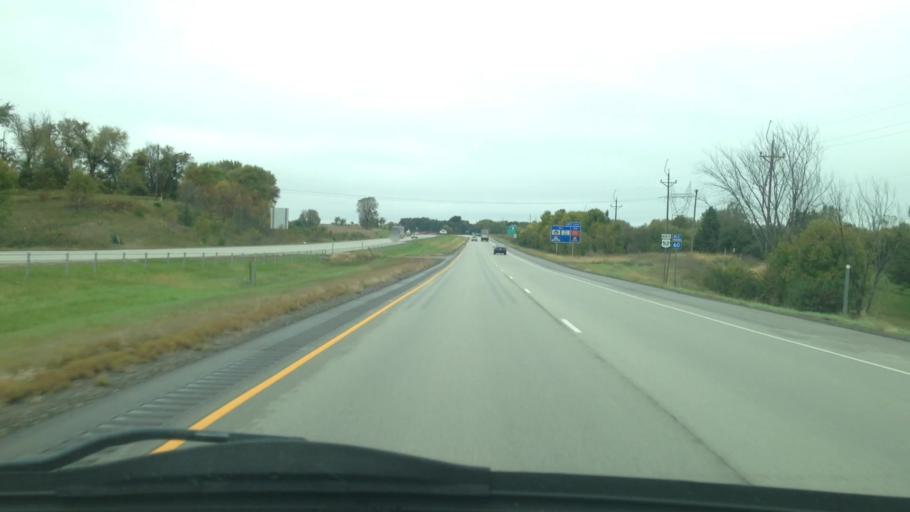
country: US
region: Minnesota
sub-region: Goodhue County
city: Zumbrota
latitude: 44.2701
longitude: -92.6538
